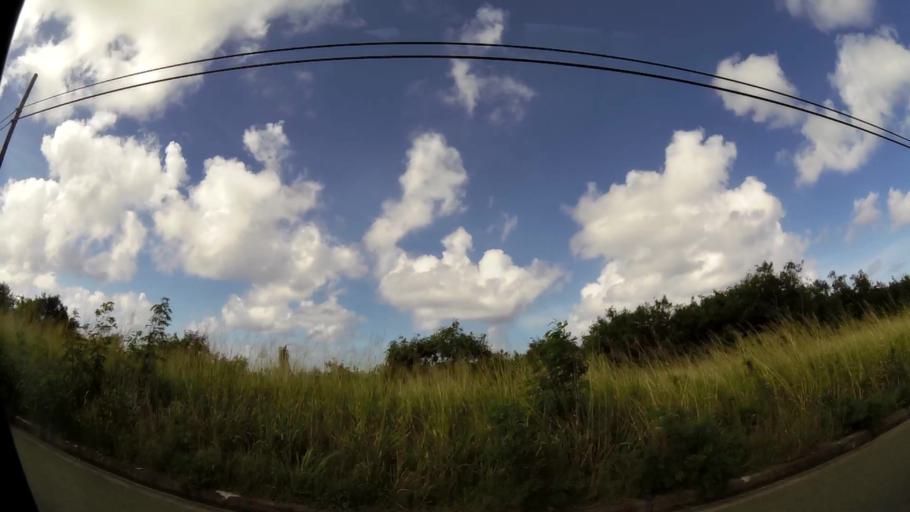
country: BB
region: Saint Lucy
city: Checker Hall
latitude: 13.2918
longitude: -59.6413
